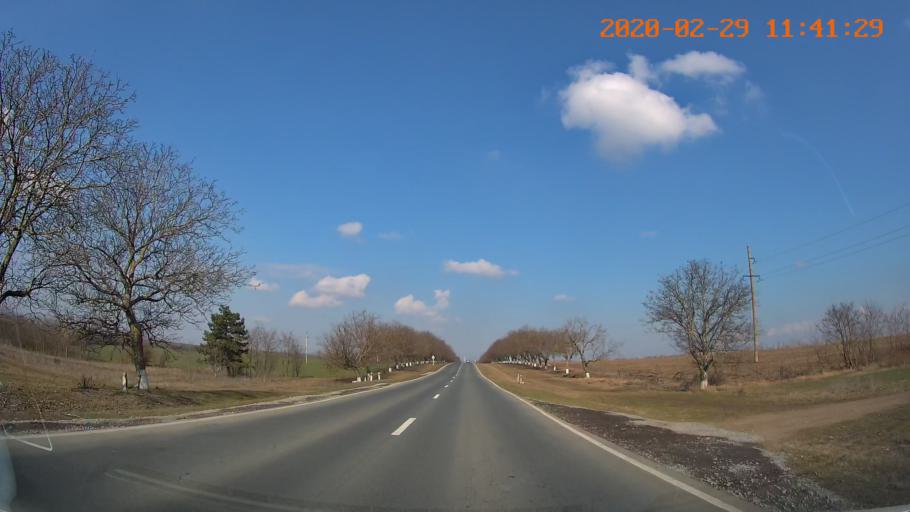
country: MD
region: Rezina
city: Saharna
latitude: 47.6719
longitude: 29.0163
